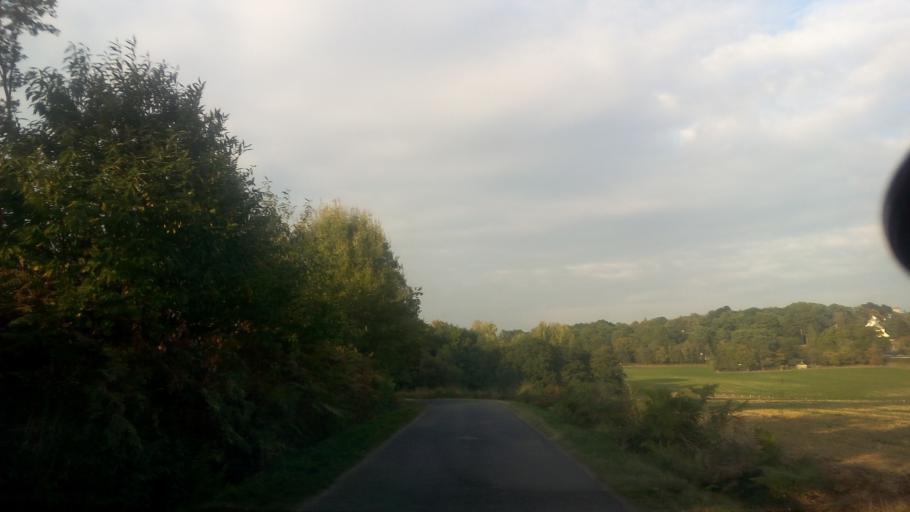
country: FR
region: Brittany
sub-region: Departement du Morbihan
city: Saint-Jean-la-Poterie
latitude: 47.6290
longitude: -2.1260
